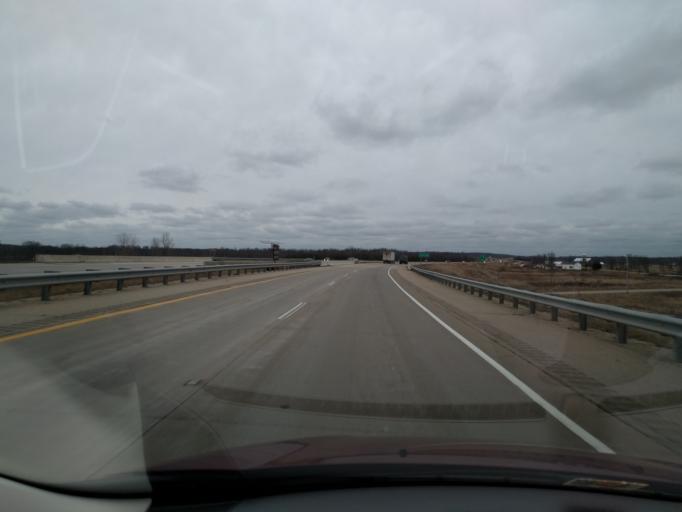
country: US
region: Wisconsin
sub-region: Winnebago County
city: Winneconne
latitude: 44.2246
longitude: -88.7061
